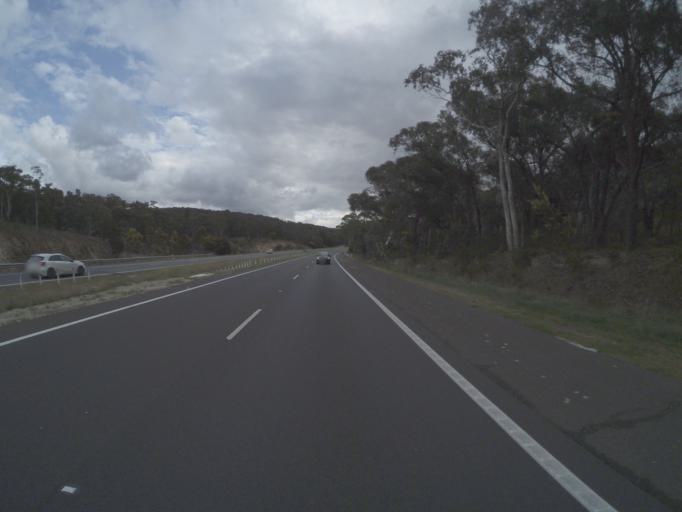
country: AU
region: New South Wales
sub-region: Goulburn Mulwaree
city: Goulburn
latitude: -34.7442
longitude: 149.9282
